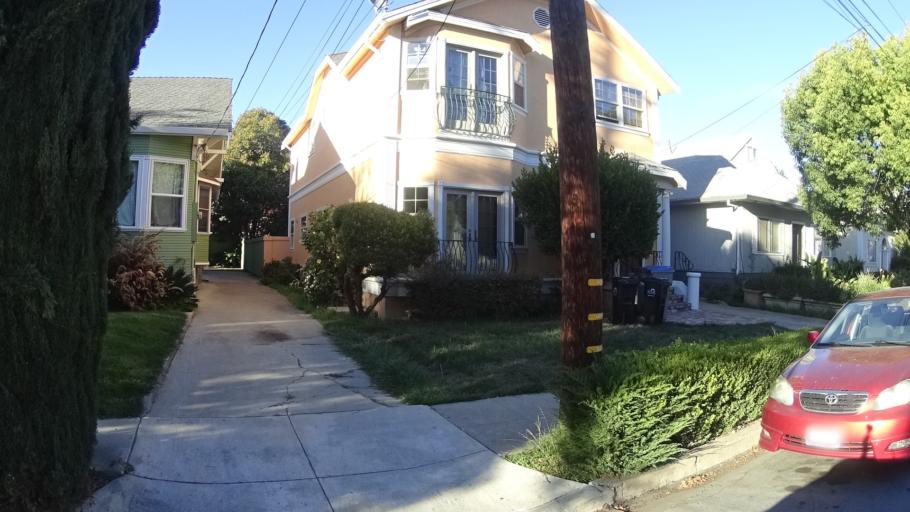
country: US
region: California
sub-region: Santa Clara County
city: San Jose
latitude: 37.3428
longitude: -121.8998
